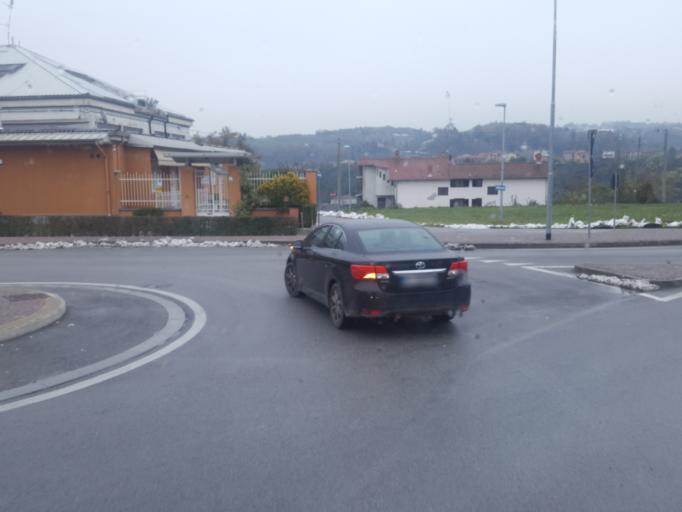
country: IT
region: Piedmont
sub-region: Provincia di Cuneo
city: Breo
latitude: 44.4033
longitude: 7.8291
